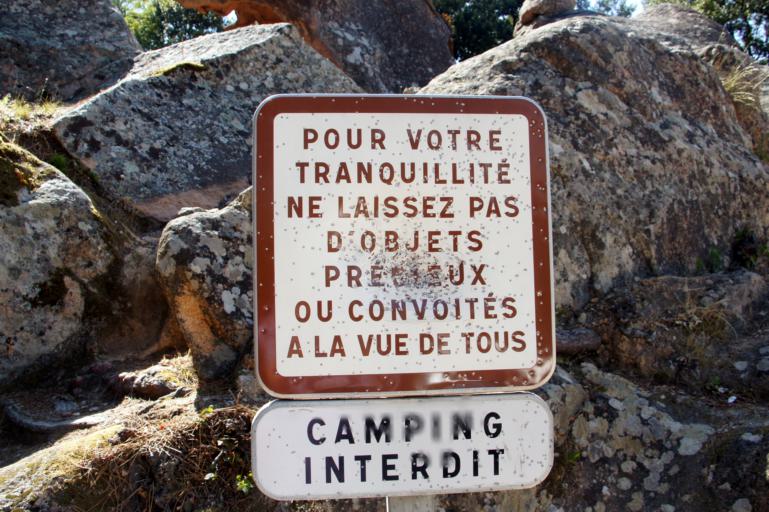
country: FR
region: Corsica
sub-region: Departement de la Corse-du-Sud
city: Cargese
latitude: 42.2515
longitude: 8.6589
